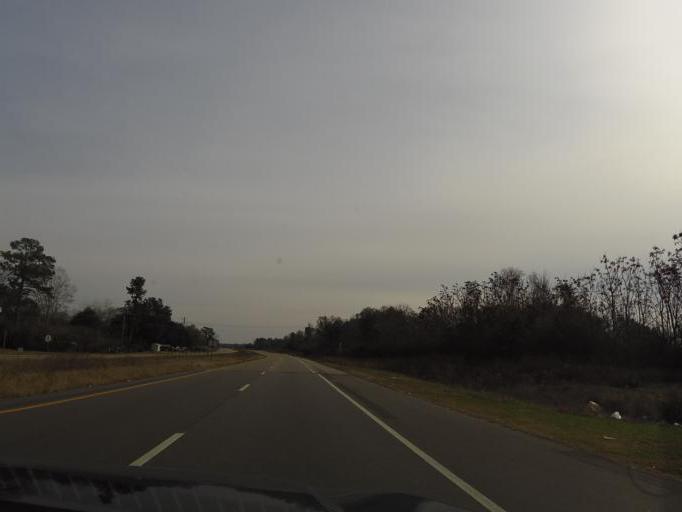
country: US
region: Alabama
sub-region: Houston County
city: Ashford
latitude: 31.1617
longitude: -85.1915
